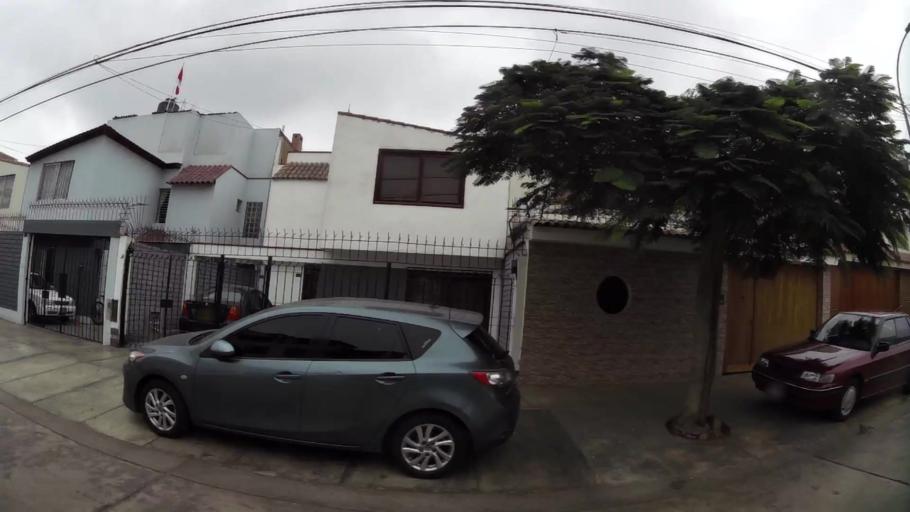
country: PE
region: Lima
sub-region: Lima
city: Surco
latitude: -12.1429
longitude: -76.9953
